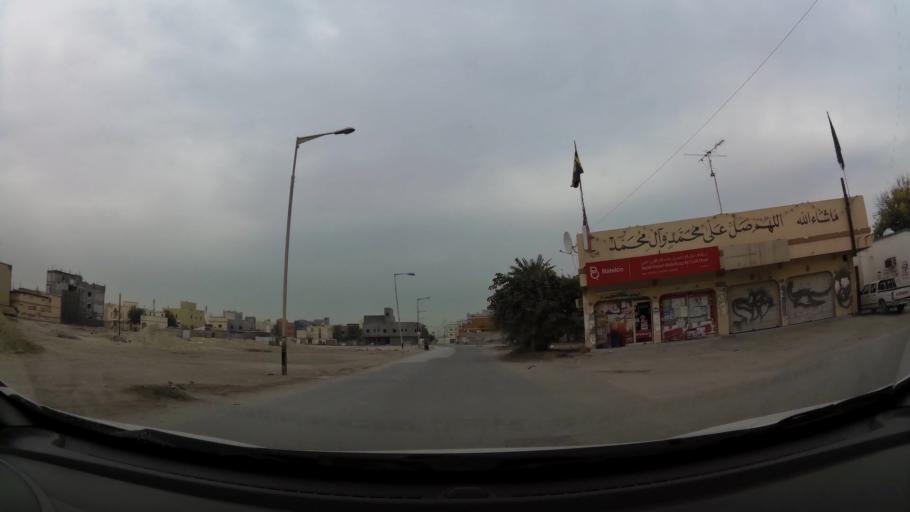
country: BH
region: Northern
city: Sitrah
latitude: 26.1412
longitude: 50.6092
